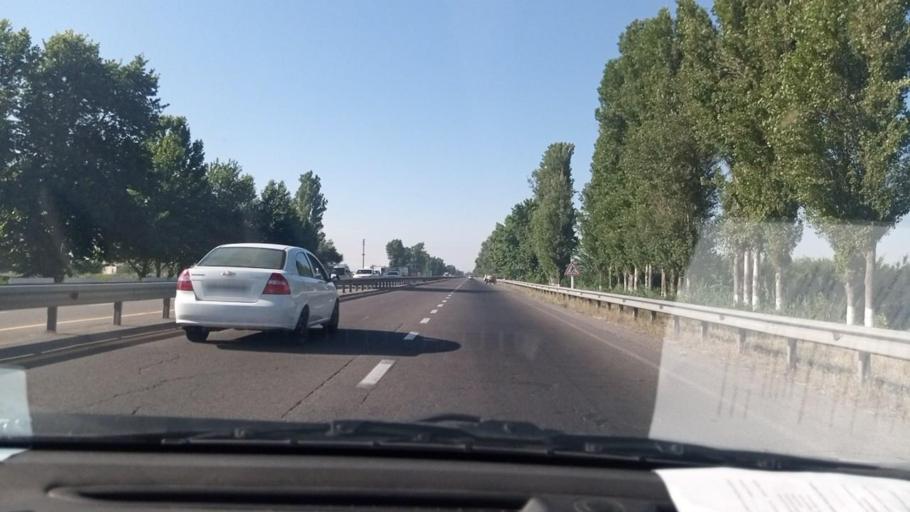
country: UZ
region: Toshkent Shahri
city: Bektemir
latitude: 41.2108
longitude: 69.4027
